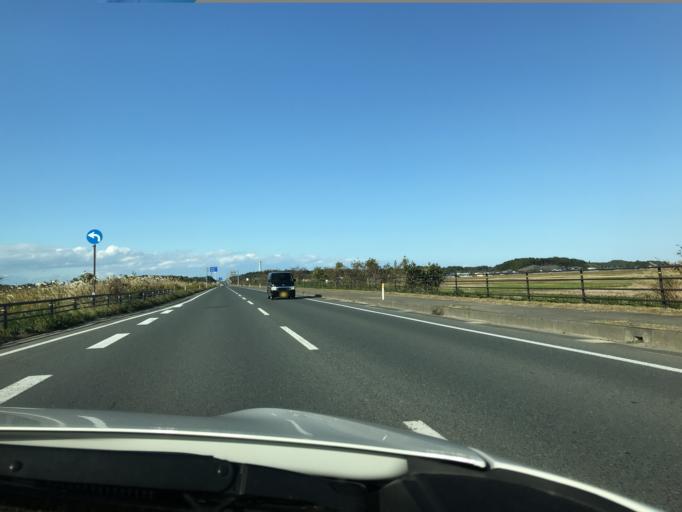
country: JP
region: Miyagi
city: Marumori
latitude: 37.7939
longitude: 140.9439
